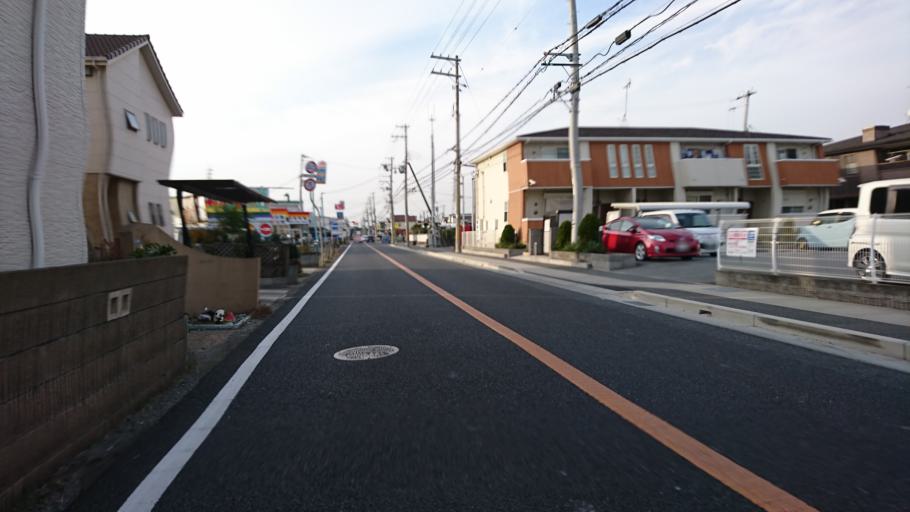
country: JP
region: Hyogo
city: Kakogawacho-honmachi
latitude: 34.7175
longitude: 134.8584
